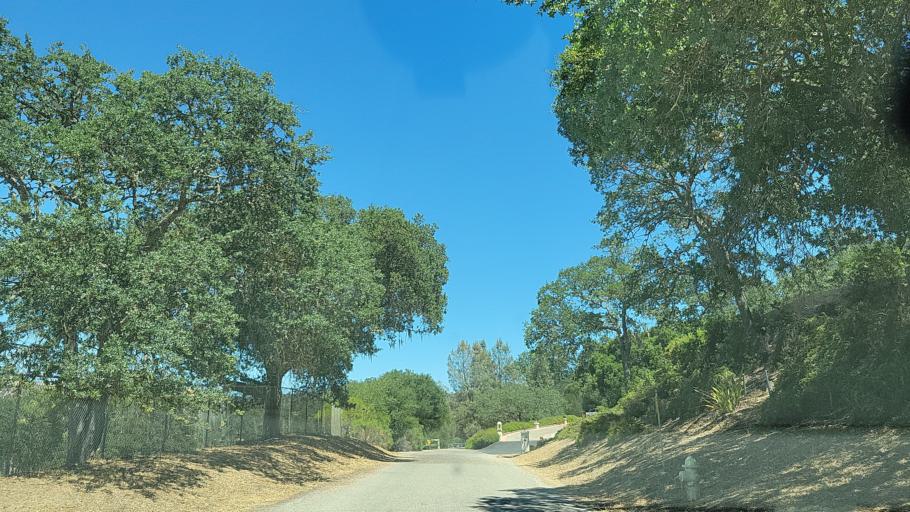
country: US
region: California
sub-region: San Luis Obispo County
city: Atascadero
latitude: 35.4692
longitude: -120.6459
